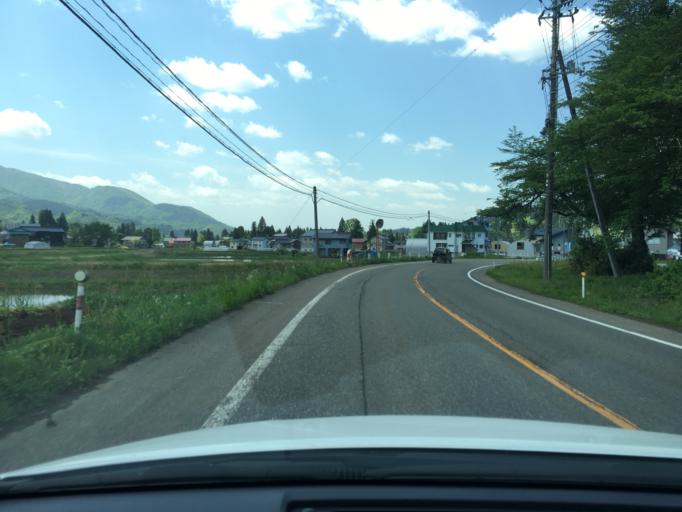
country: JP
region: Niigata
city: Tochio-honcho
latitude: 37.3353
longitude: 139.0338
